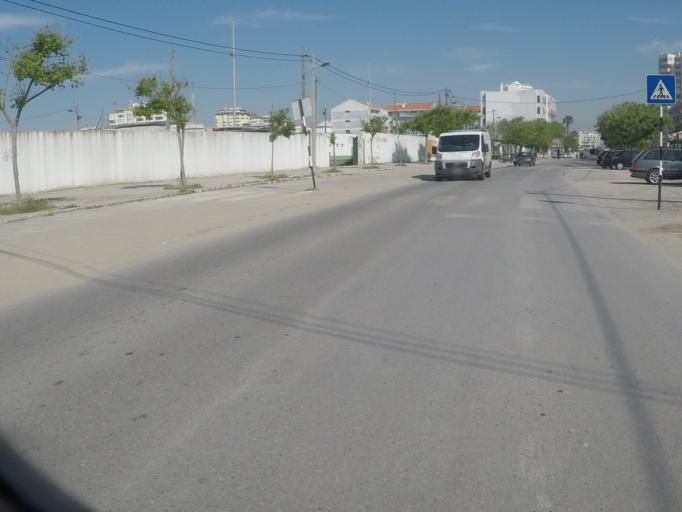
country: PT
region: Setubal
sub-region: Almada
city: Costa de Caparica
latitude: 38.6369
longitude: -9.2292
